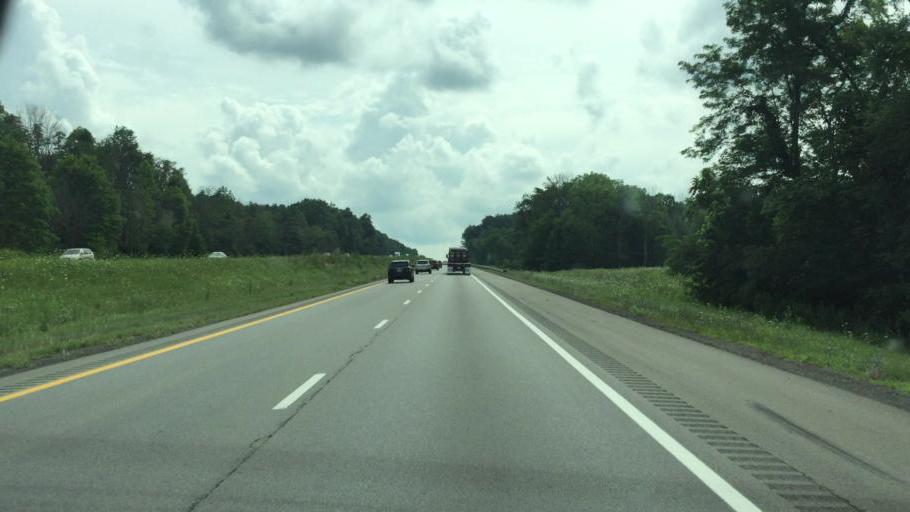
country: US
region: Ohio
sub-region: Muskingum County
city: Zanesville
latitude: 39.9528
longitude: -82.1872
